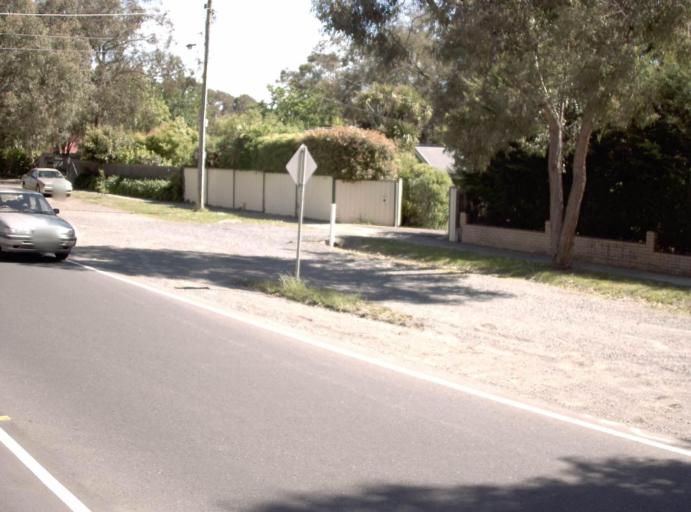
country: AU
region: Victoria
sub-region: Maroondah
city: Croydon South
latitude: -37.8152
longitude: 145.2693
